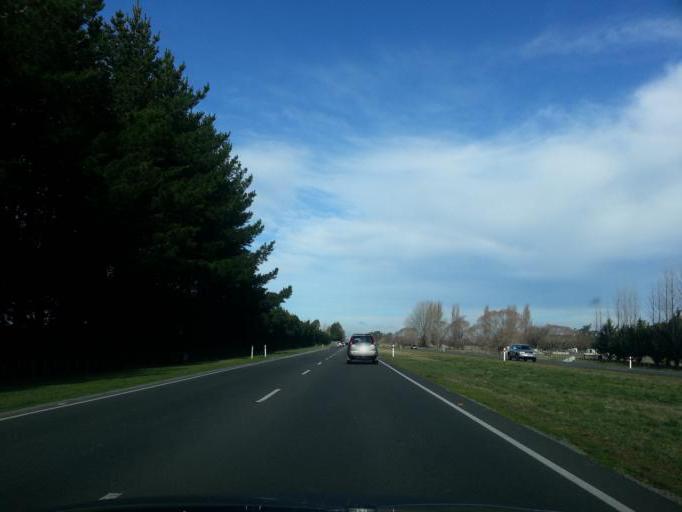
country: NZ
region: Canterbury
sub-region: Waimakariri District
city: Kaiapoi
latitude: -43.3954
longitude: 172.6410
